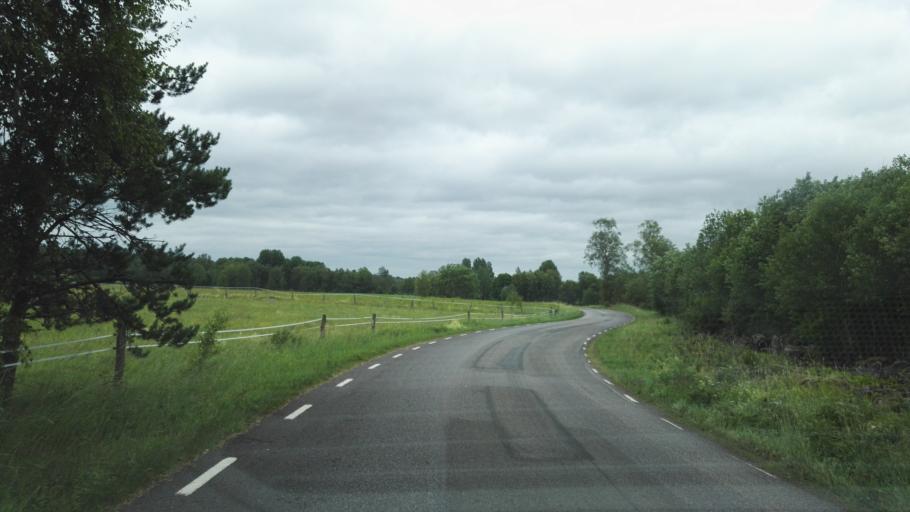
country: SE
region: Kronoberg
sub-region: Vaxjo Kommun
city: Rottne
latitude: 57.1749
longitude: 14.7849
